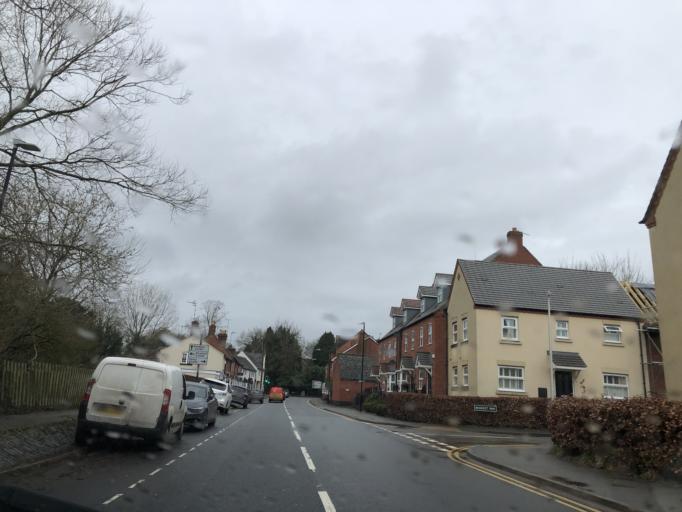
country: GB
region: England
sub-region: Warwickshire
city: Henley in Arden
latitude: 52.2875
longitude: -1.7788
